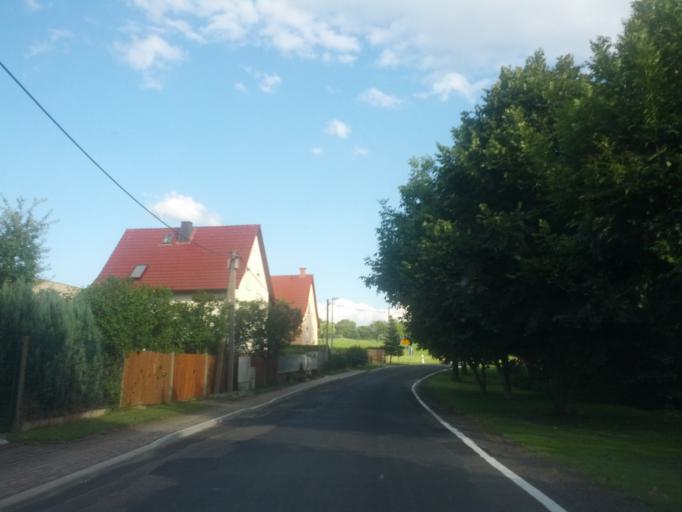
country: DE
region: Thuringia
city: Bischofroda
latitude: 51.0168
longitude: 10.3961
